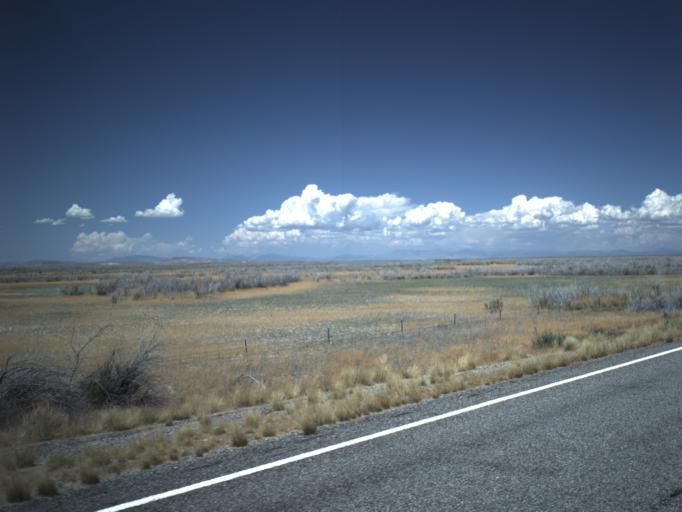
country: US
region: Utah
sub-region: Millard County
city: Delta
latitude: 39.2607
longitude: -112.8795
